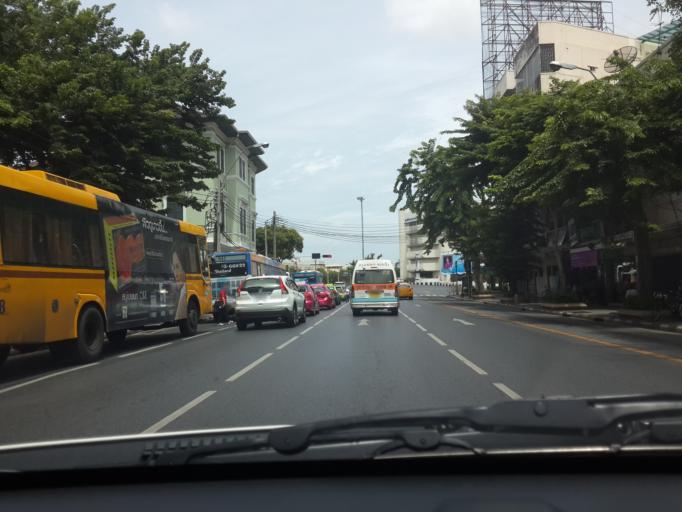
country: TH
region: Bangkok
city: Bangkok
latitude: 13.7564
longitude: 100.5070
